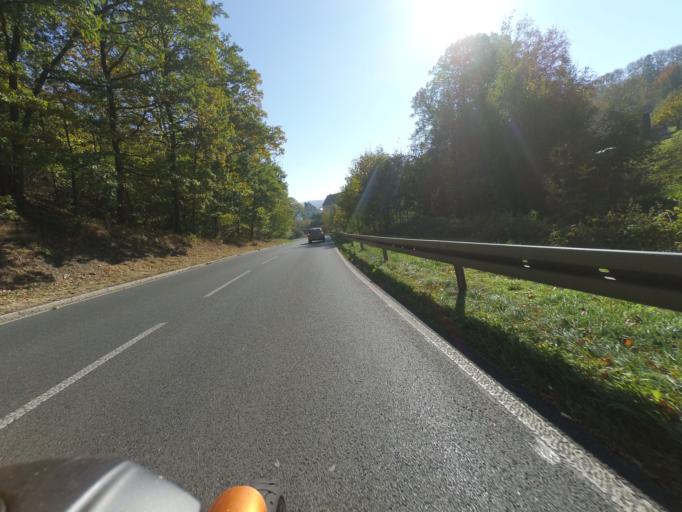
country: DE
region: Saxony
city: Glashutte
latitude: 50.8565
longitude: 13.7614
